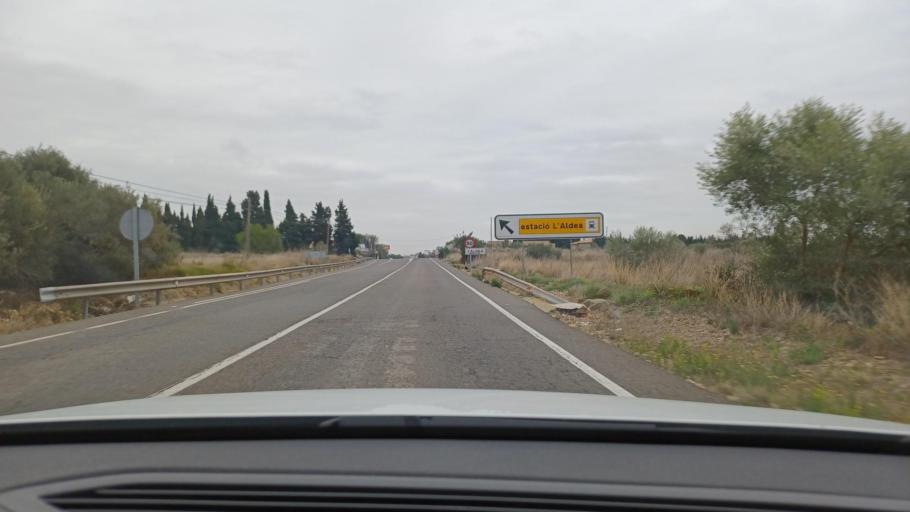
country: ES
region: Catalonia
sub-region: Provincia de Tarragona
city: Amposta
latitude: 40.7513
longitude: 0.6111
